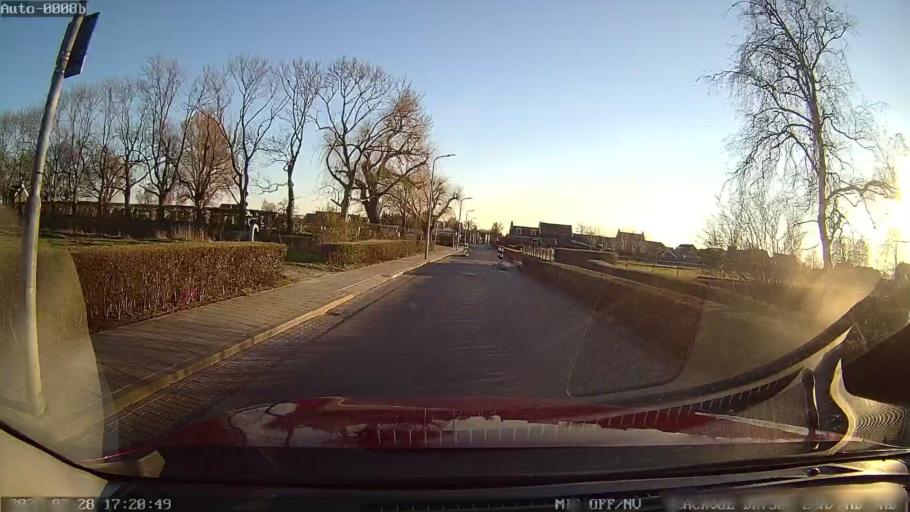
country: NL
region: Zeeland
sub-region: Schouwen-Duiveland
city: Bruinisse
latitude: 51.6877
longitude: 3.9810
